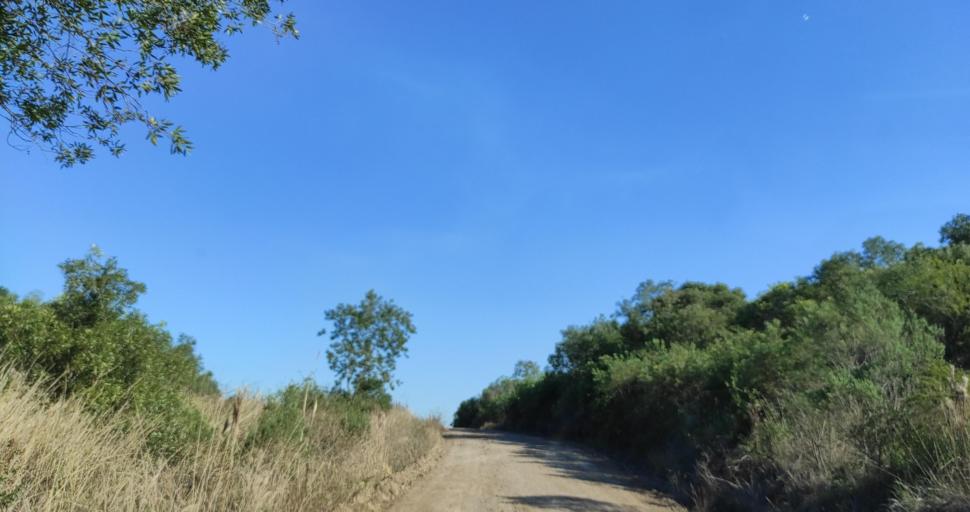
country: AR
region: Misiones
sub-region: Departamento de Apostoles
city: San Jose
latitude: -27.6682
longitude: -55.6606
